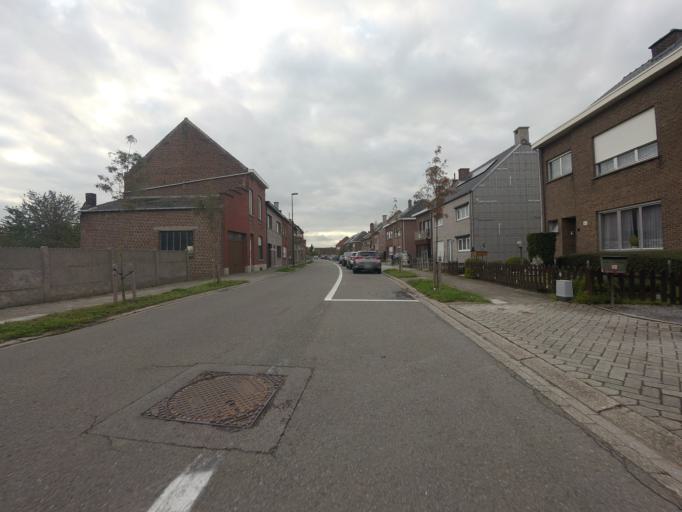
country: BE
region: Flanders
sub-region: Provincie Vlaams-Brabant
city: Machelen
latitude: 50.9303
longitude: 4.4565
